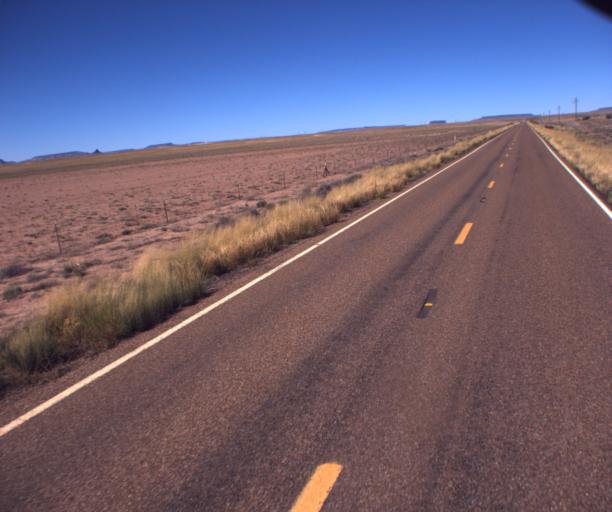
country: US
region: Arizona
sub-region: Navajo County
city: Holbrook
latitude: 35.0965
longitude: -110.0964
